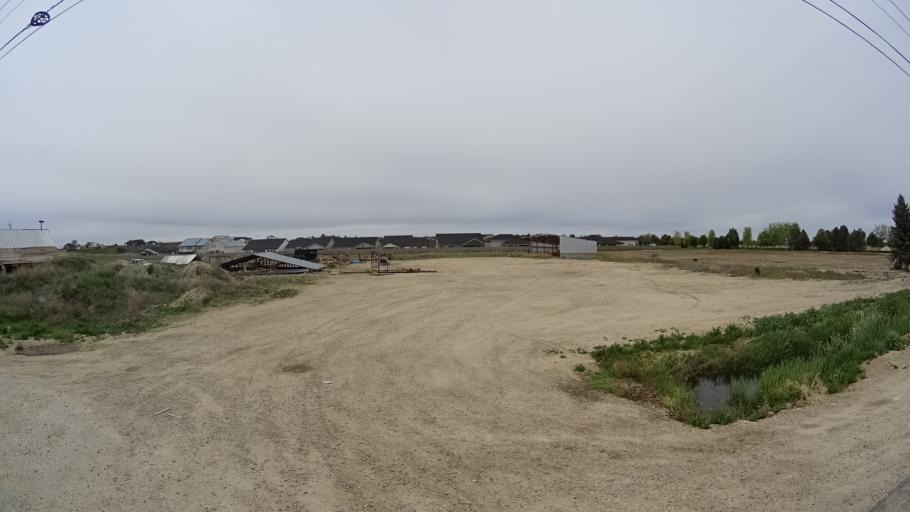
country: US
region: Idaho
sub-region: Ada County
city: Meridian
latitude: 43.5525
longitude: -116.3544
